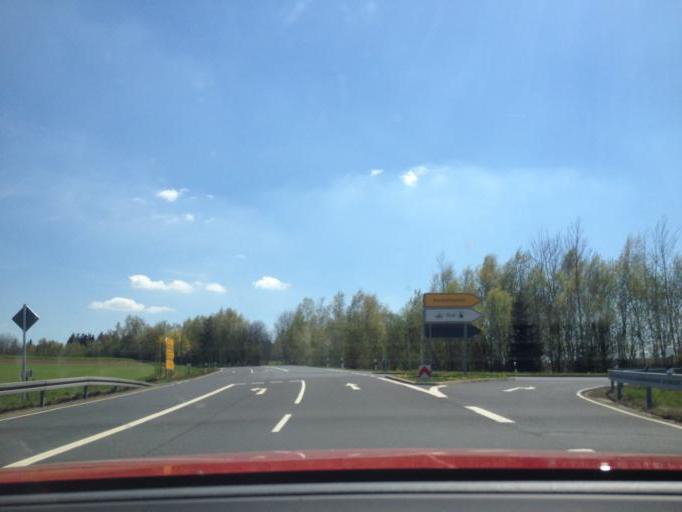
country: DE
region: Bavaria
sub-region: Upper Franconia
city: Kirchenlamitz
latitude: 50.1482
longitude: 11.9593
